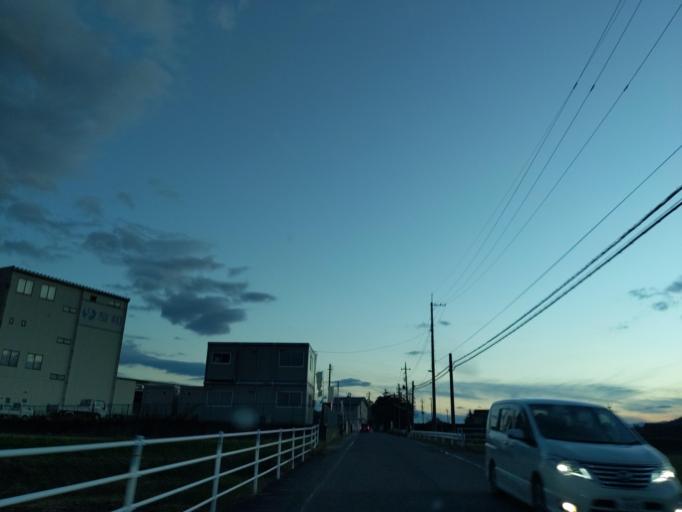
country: JP
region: Fukushima
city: Motomiya
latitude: 37.4964
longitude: 140.3848
